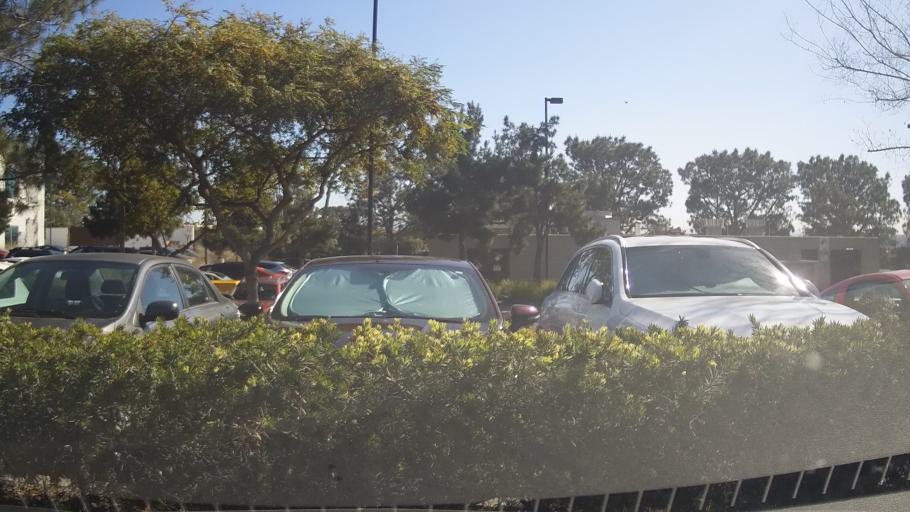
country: US
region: California
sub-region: San Diego County
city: La Jolla
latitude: 32.8932
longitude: -117.2378
